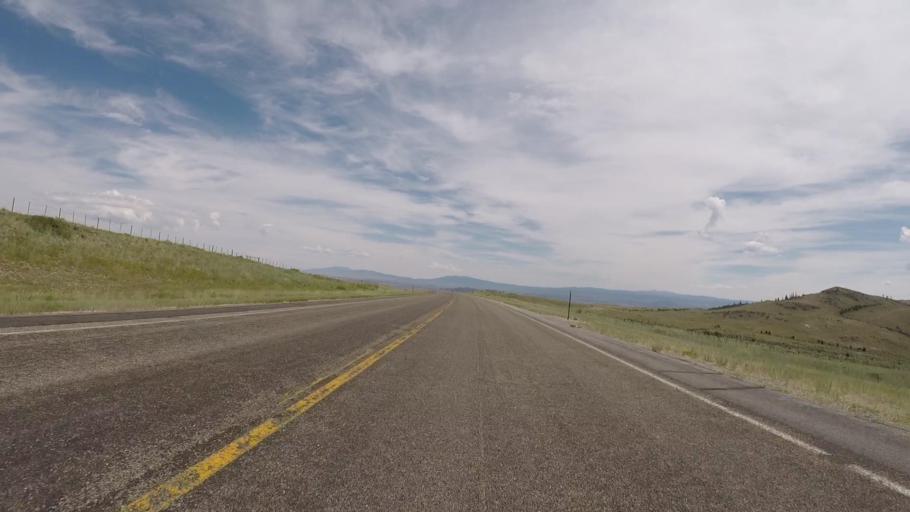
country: US
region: Wyoming
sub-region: Carbon County
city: Saratoga
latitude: 41.1886
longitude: -106.8550
